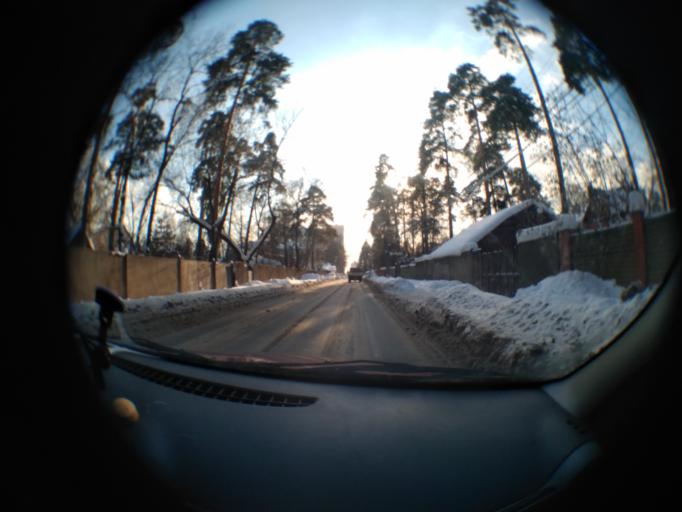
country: RU
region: Moskovskaya
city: Bykovo
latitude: 55.6136
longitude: 38.0910
